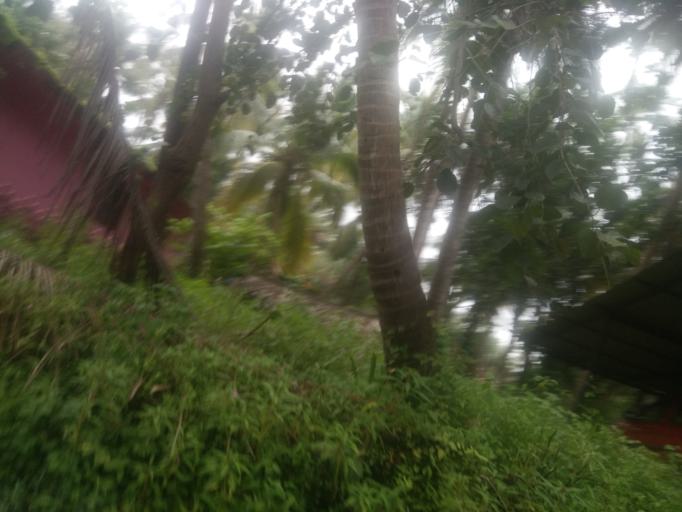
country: IN
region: Goa
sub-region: South Goa
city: Cuncolim
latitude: 15.1770
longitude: 73.9689
